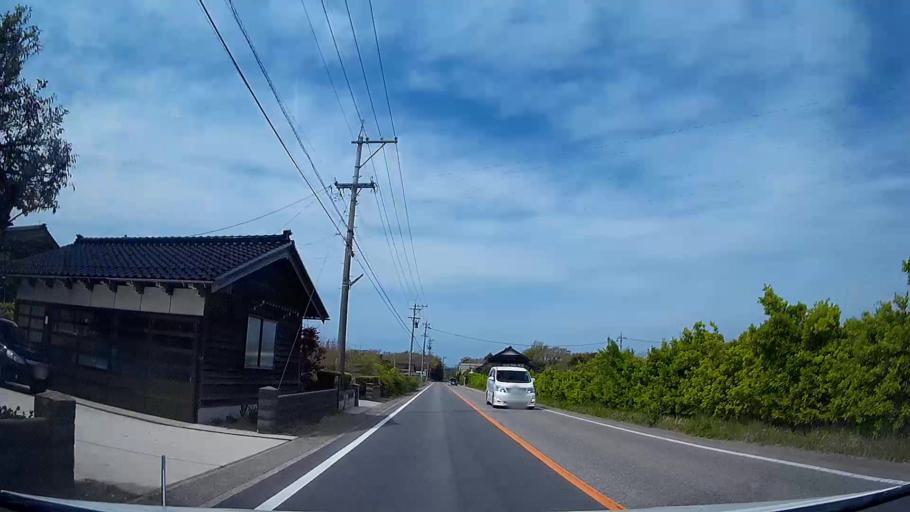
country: JP
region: Ishikawa
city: Hakui
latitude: 36.9669
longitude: 136.7726
